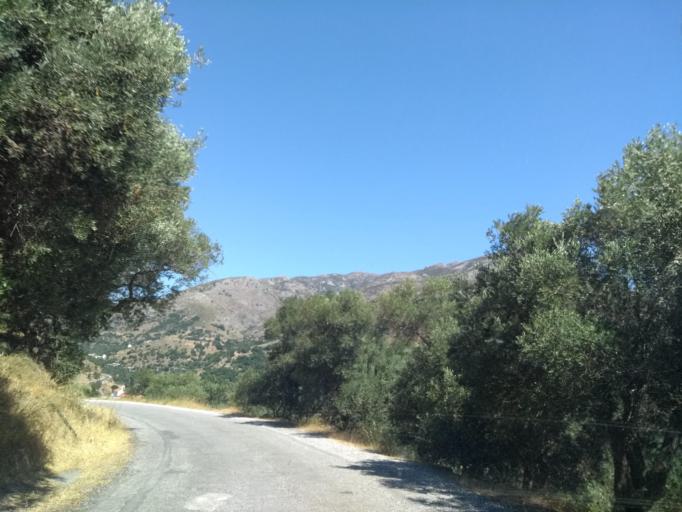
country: GR
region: Crete
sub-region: Nomos Chanias
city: Vryses
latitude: 35.3632
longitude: 23.5939
